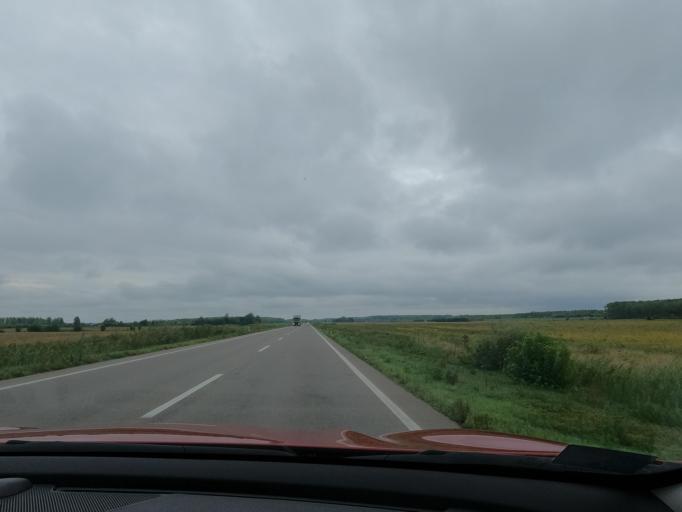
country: RS
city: Taras
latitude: 45.3933
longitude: 20.1785
